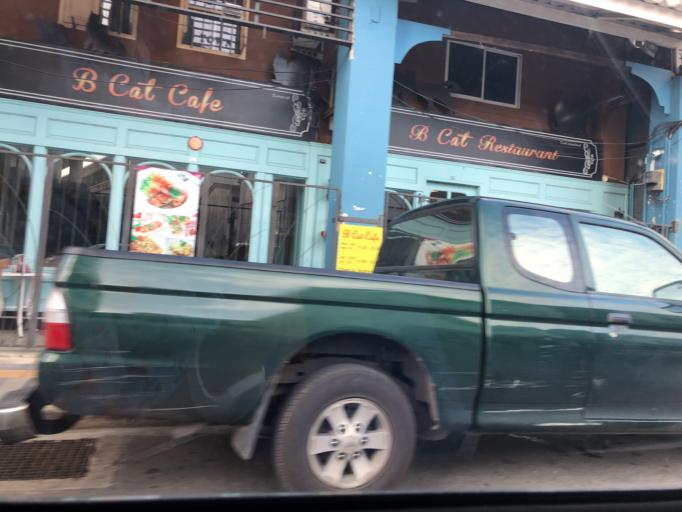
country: TH
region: Phuket
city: Ban Talat Nua
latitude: 7.8855
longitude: 98.3907
